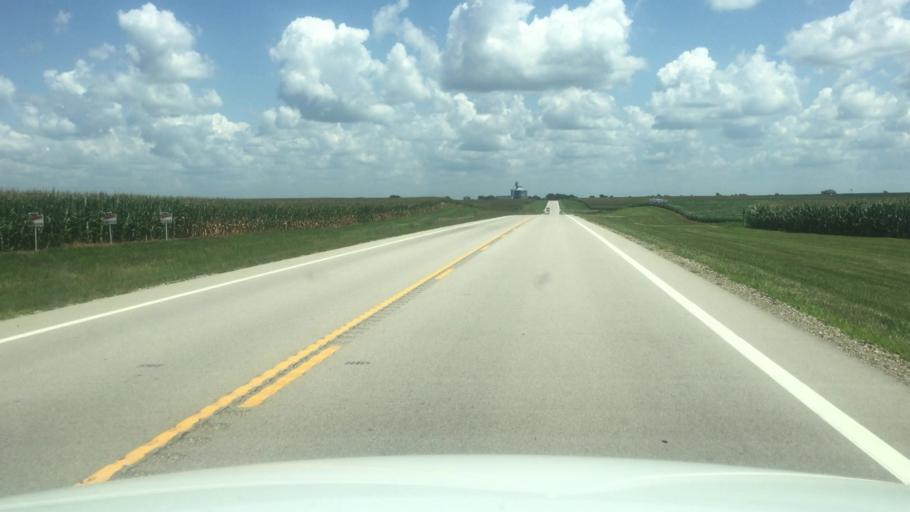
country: US
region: Kansas
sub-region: Brown County
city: Horton
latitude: 39.6603
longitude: -95.4027
